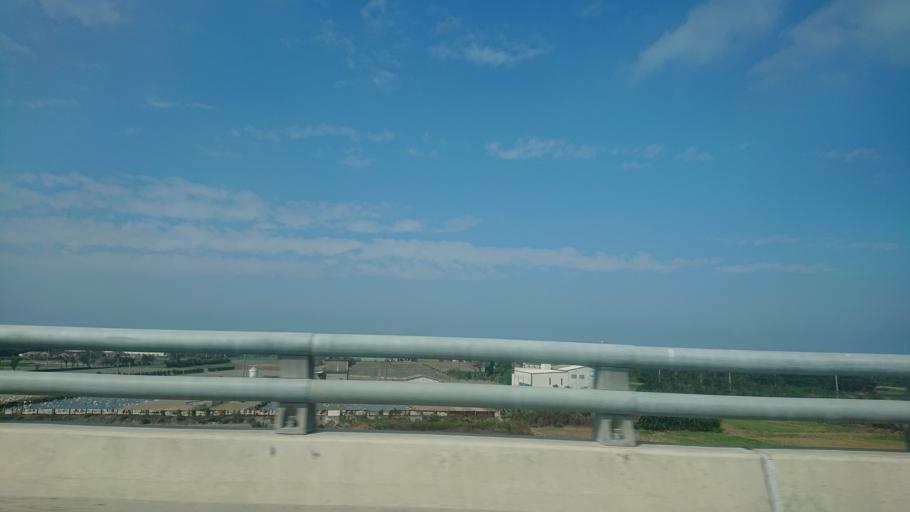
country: TW
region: Taiwan
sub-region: Changhua
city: Chang-hua
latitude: 23.9967
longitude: 120.3786
